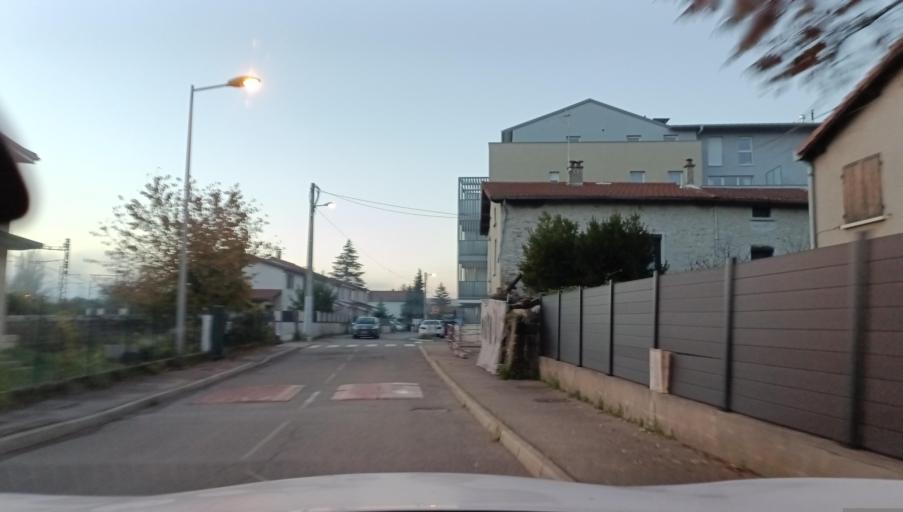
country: FR
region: Rhone-Alpes
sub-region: Departement de l'Isere
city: Chasse-sur-Rhone
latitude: 45.5763
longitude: 4.8107
